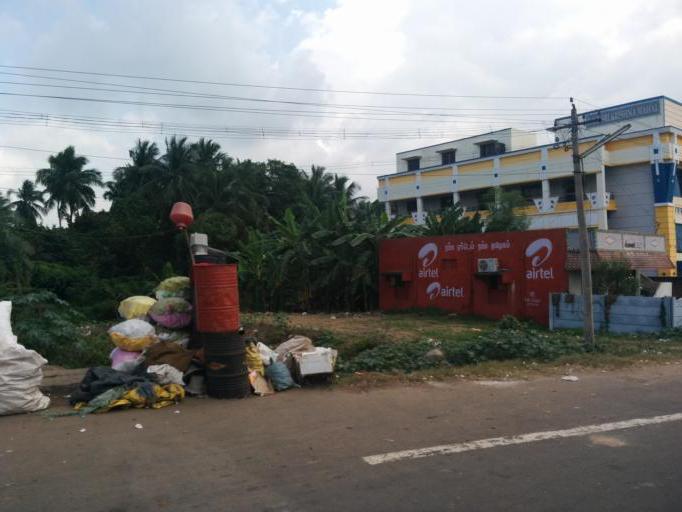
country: IN
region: Tamil Nadu
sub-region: Kancheepuram
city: Madurantakam
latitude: 12.5326
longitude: 79.9009
